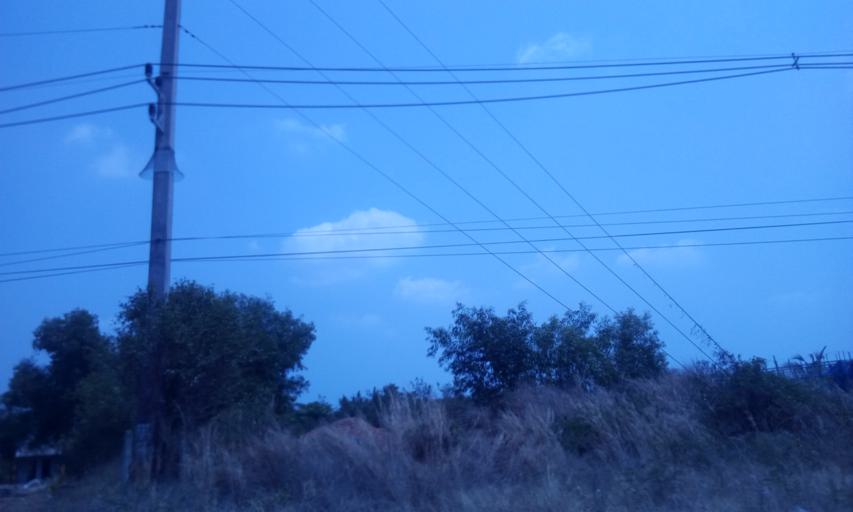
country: TH
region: Chachoengsao
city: Bang Nam Priao
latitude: 13.8347
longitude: 101.0550
